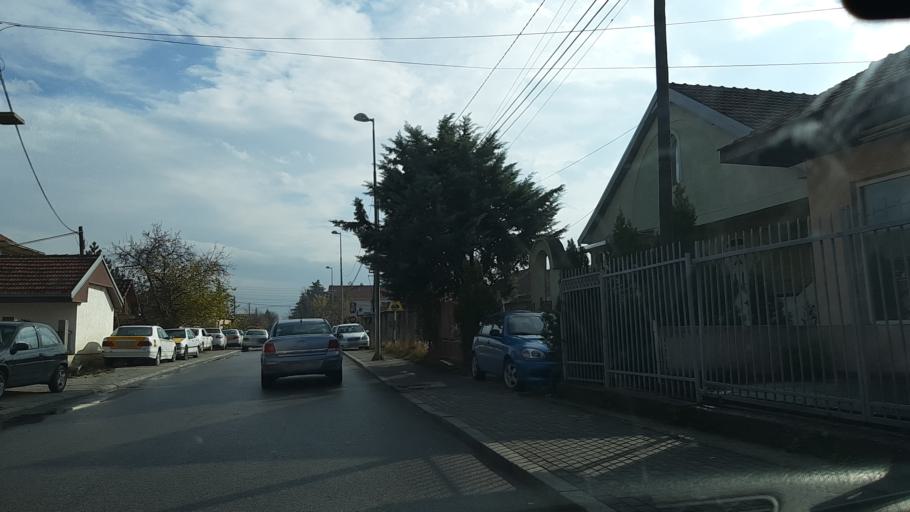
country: MK
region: Kisela Voda
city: Usje
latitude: 41.9779
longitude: 21.4827
